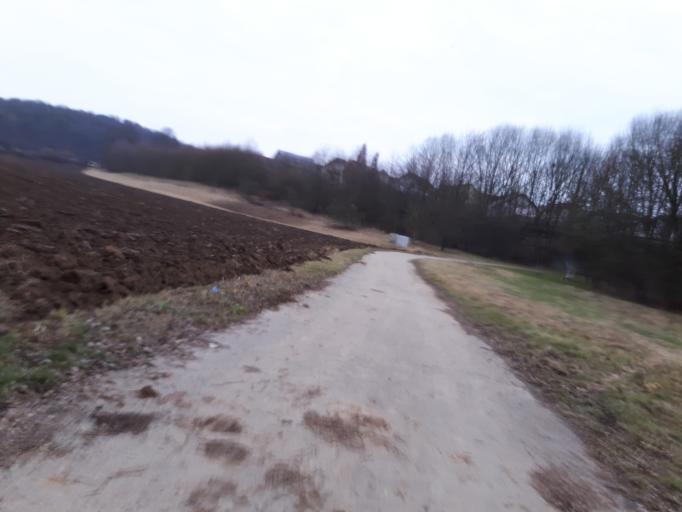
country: DE
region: Baden-Wuerttemberg
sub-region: Regierungsbezirk Stuttgart
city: Neckarsulm
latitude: 49.2143
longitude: 9.2366
